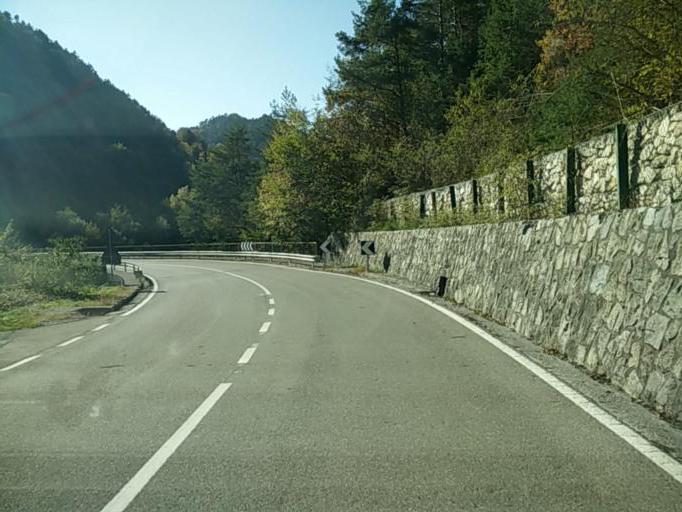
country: IT
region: Lombardy
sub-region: Provincia di Brescia
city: Anfo
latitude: 45.7496
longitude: 10.5089
